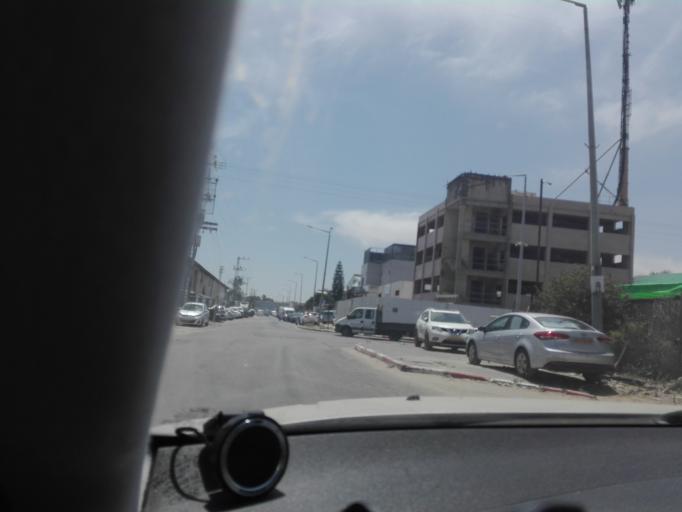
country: IL
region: Central District
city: Bene 'Ayish
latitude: 31.7372
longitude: 34.7527
